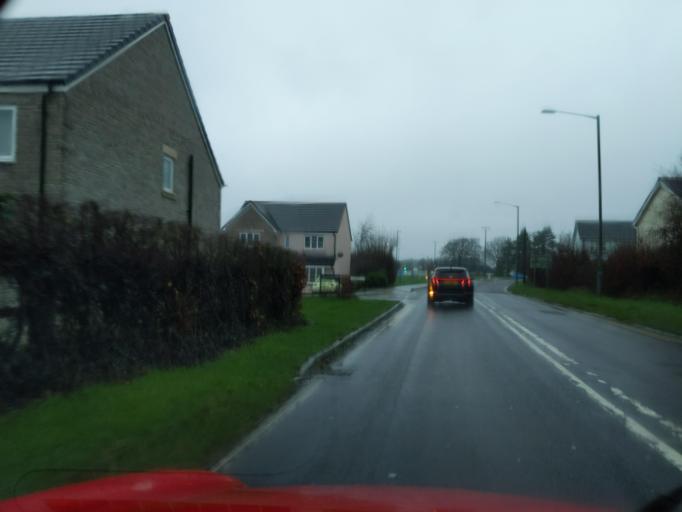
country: GB
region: England
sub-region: Cornwall
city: Launceston
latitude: 50.6280
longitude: -4.3455
